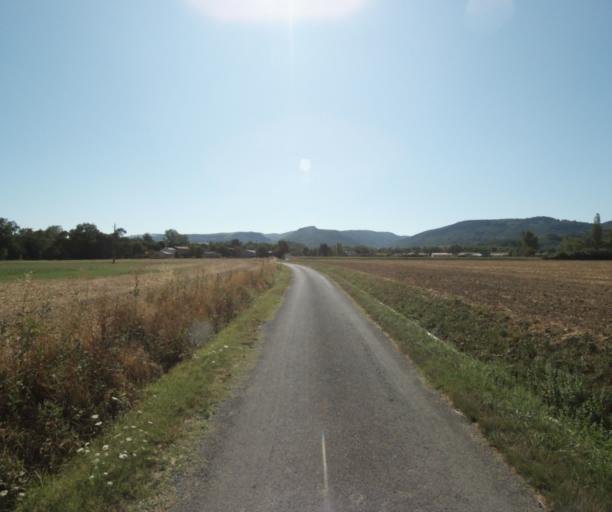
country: FR
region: Midi-Pyrenees
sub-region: Departement de la Haute-Garonne
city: Revel
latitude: 43.4567
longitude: 2.0346
